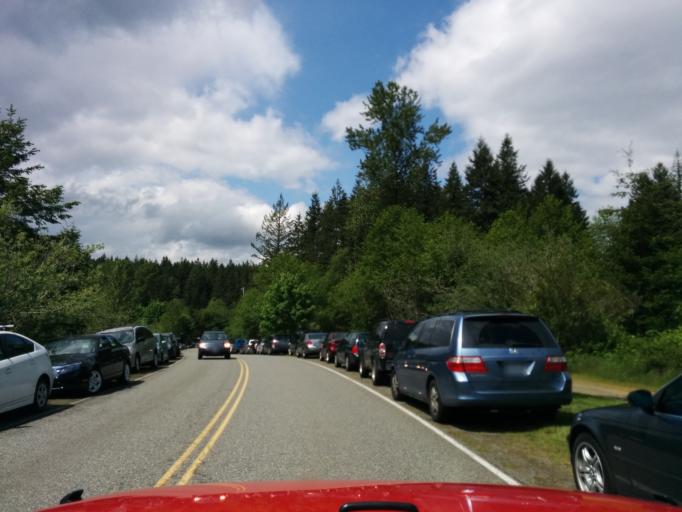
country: US
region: Washington
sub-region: King County
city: Riverbend
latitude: 47.4339
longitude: -121.7671
